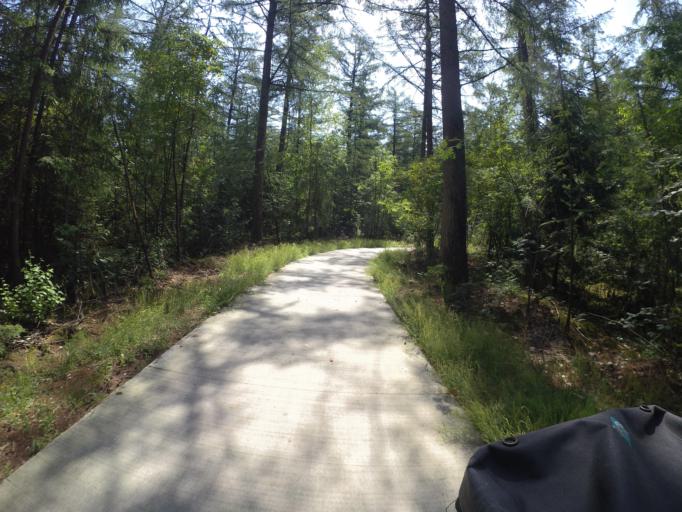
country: NL
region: Drenthe
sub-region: Gemeente De Wolden
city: Ruinen
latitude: 52.7254
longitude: 6.3602
